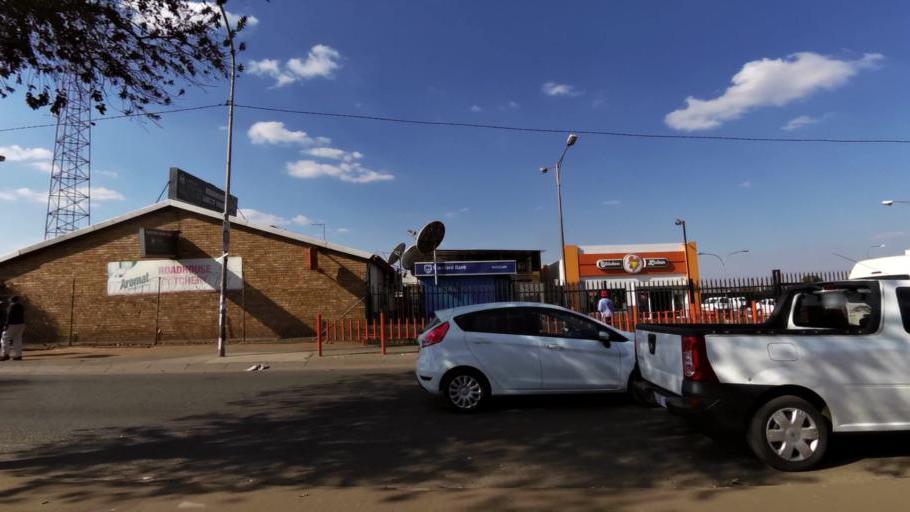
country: ZA
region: Gauteng
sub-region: City of Johannesburg Metropolitan Municipality
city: Roodepoort
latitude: -26.2154
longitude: 27.8710
